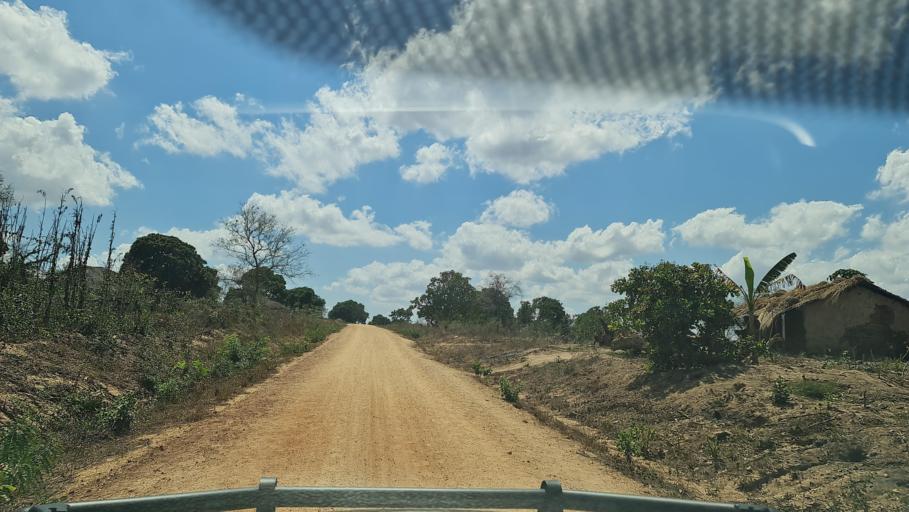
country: MZ
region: Nampula
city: Nacala
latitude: -14.1743
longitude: 40.2383
